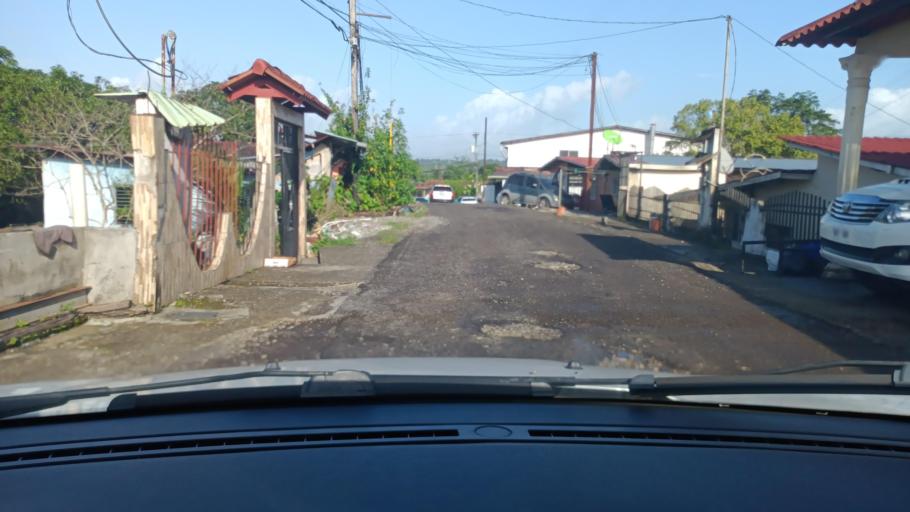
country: PA
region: Colon
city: Sabanitas
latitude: 9.3454
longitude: -79.8026
